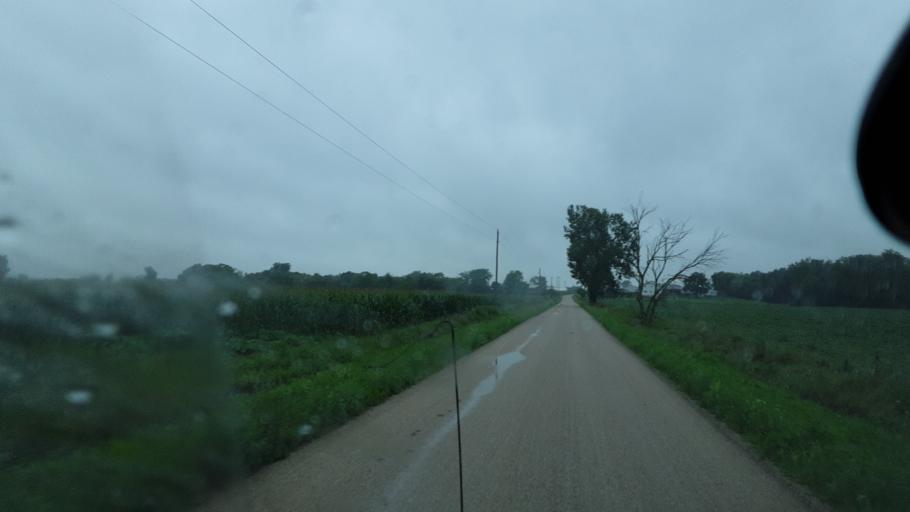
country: US
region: Indiana
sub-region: Adams County
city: Berne
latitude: 40.7032
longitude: -84.8343
